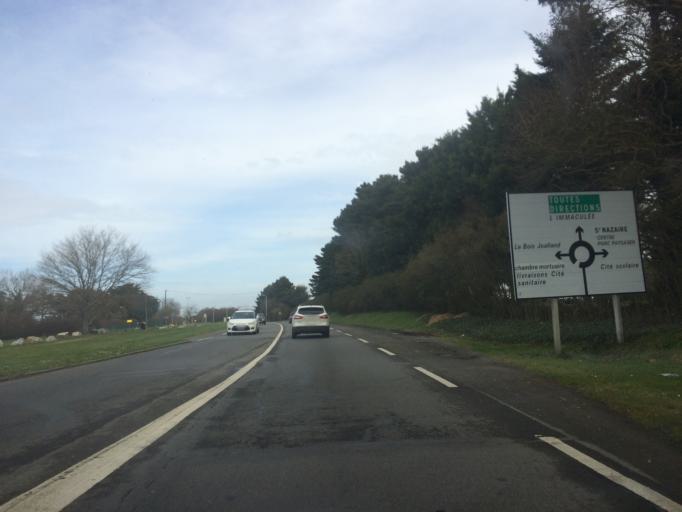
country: FR
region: Pays de la Loire
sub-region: Departement de la Loire-Atlantique
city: Saint-Nazaire
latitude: 47.2686
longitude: -2.2522
